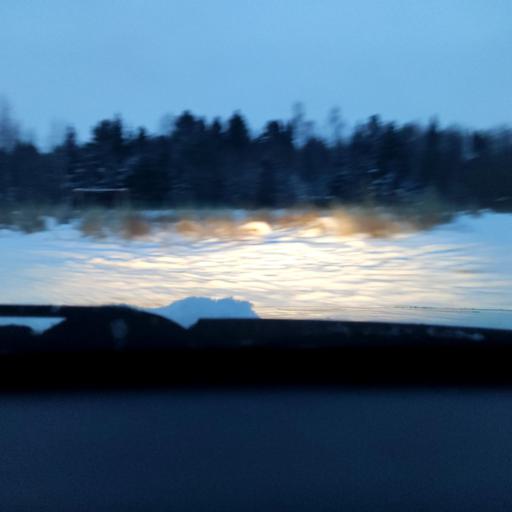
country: RU
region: Perm
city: Froly
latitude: 57.9461
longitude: 56.2308
